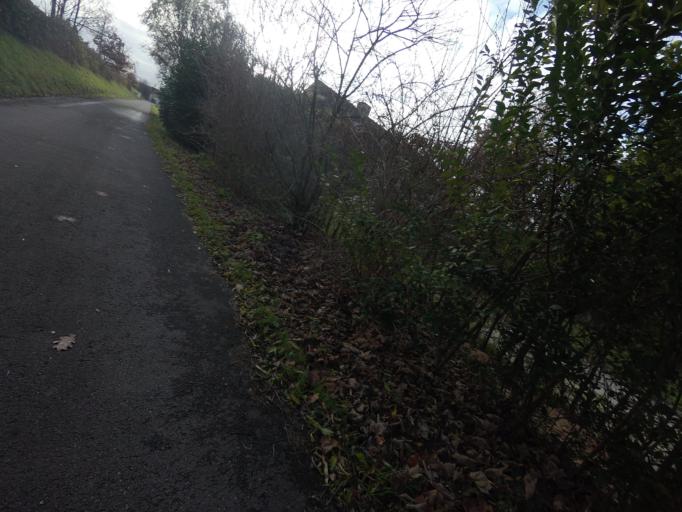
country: BE
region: Flanders
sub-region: Provincie Antwerpen
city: Schelle
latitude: 51.1301
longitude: 4.3391
